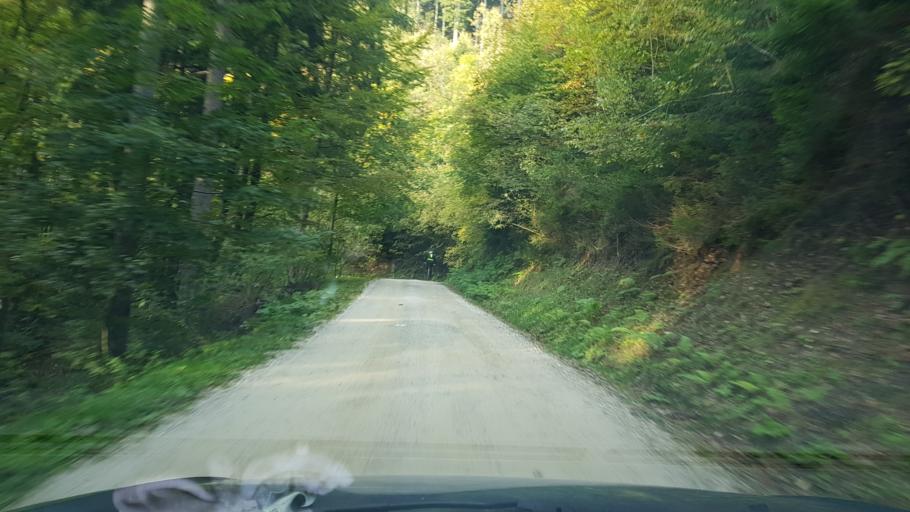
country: SI
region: Slovenj Gradec
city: Legen
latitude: 46.5246
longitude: 15.1363
